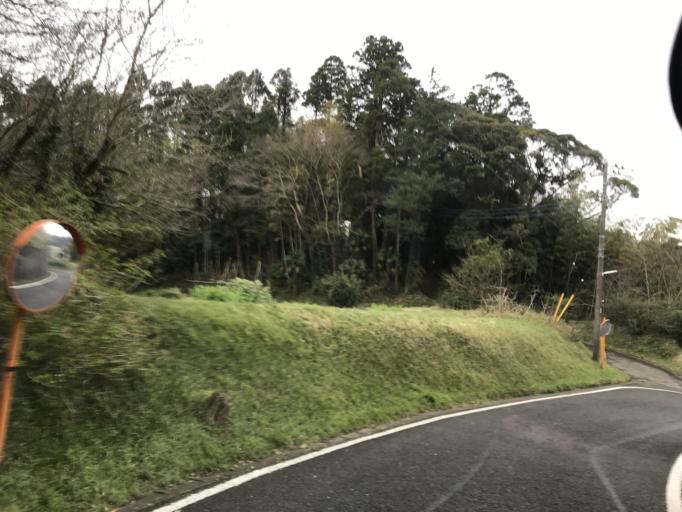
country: JP
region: Chiba
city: Sawara
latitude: 35.8098
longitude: 140.5062
